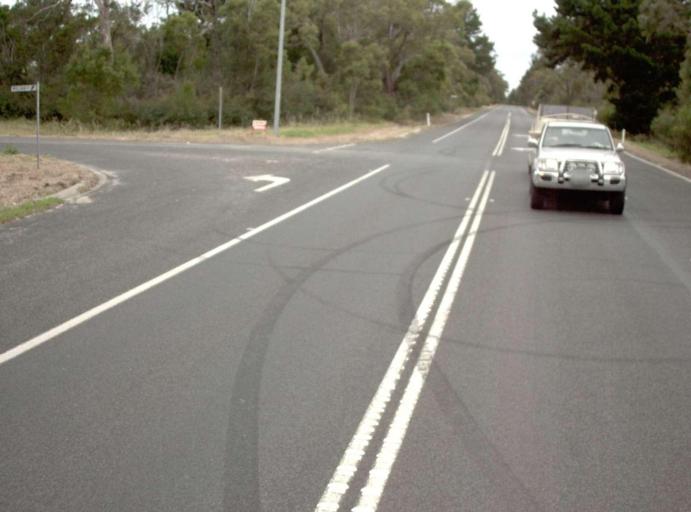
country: AU
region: Victoria
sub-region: Wellington
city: Sale
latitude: -38.1846
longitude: 147.0815
